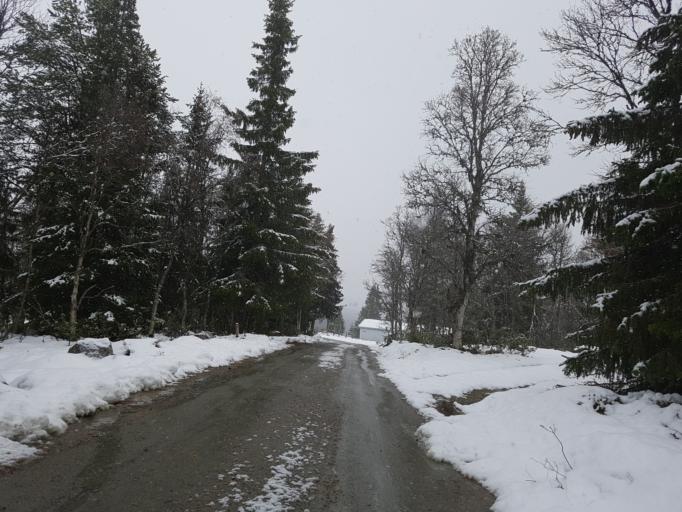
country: NO
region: Oppland
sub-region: Sel
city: Otta
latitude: 61.7897
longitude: 9.7198
